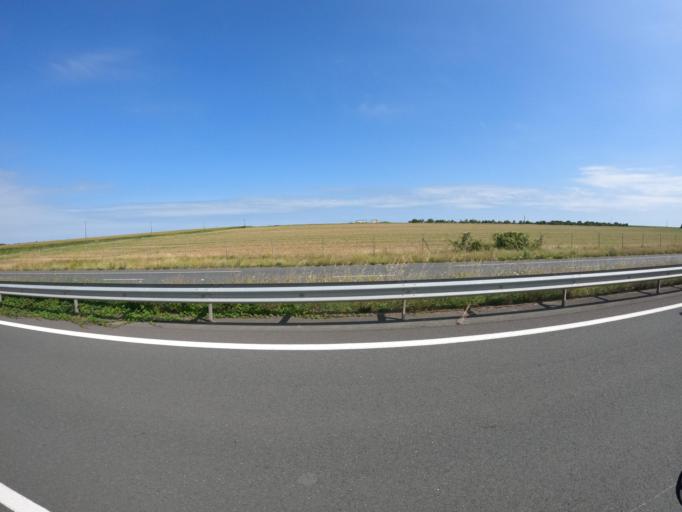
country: FR
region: Poitou-Charentes
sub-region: Departement des Deux-Sevres
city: Mauze-sur-le-Mignon
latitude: 46.1998
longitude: -0.7078
